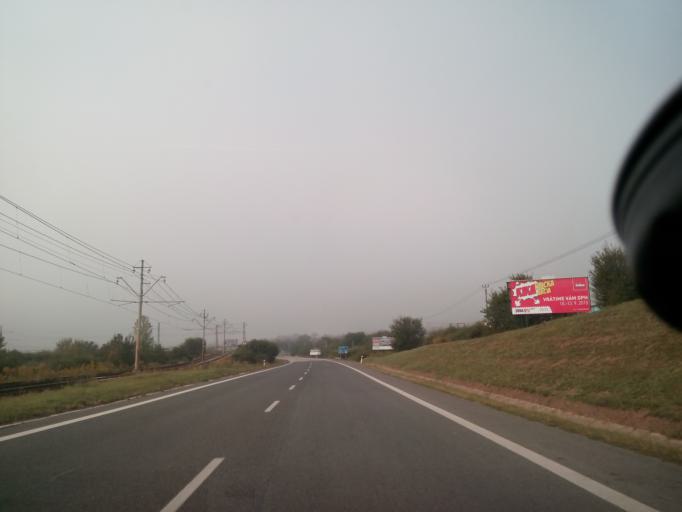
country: SK
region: Kosicky
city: Kosice
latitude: 48.6886
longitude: 21.2241
